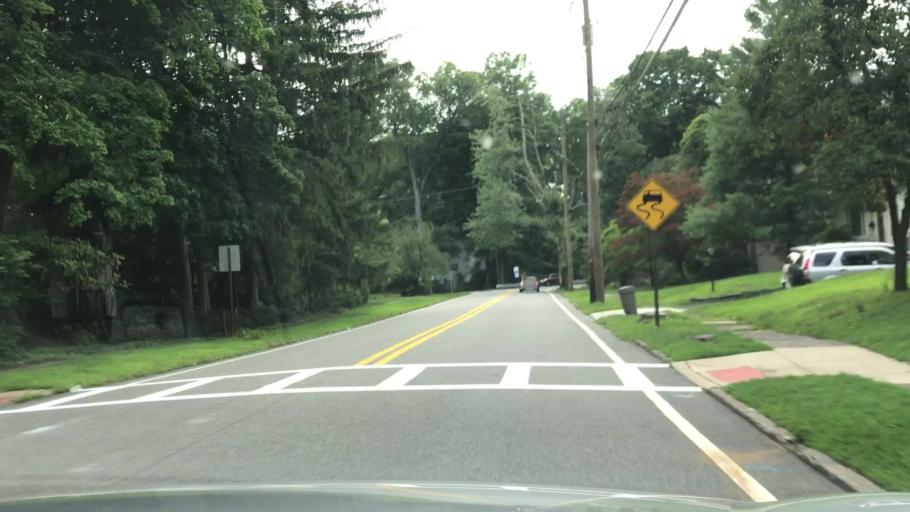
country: US
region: New Jersey
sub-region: Bergen County
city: Harrington Park
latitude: 40.9844
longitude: -73.9878
